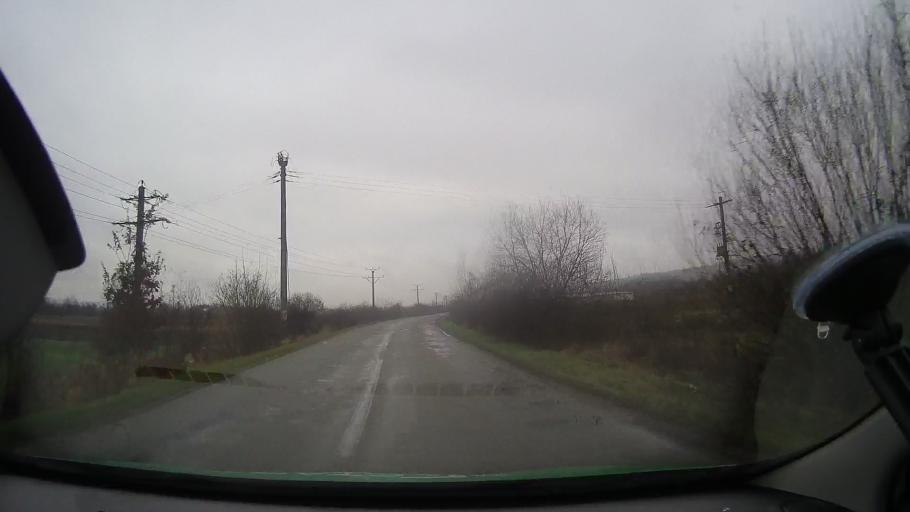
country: RO
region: Arad
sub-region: Comuna Dezna
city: Dezna
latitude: 46.4058
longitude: 22.2123
